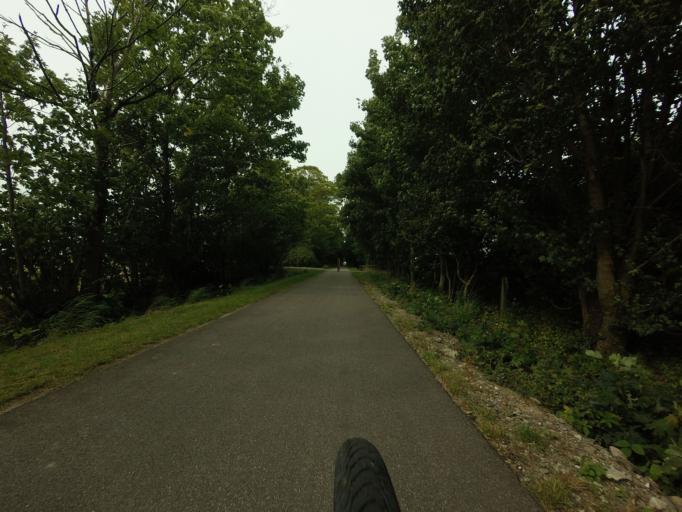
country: DK
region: Zealand
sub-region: Naestved Kommune
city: Fuglebjerg
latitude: 55.2709
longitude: 11.4703
